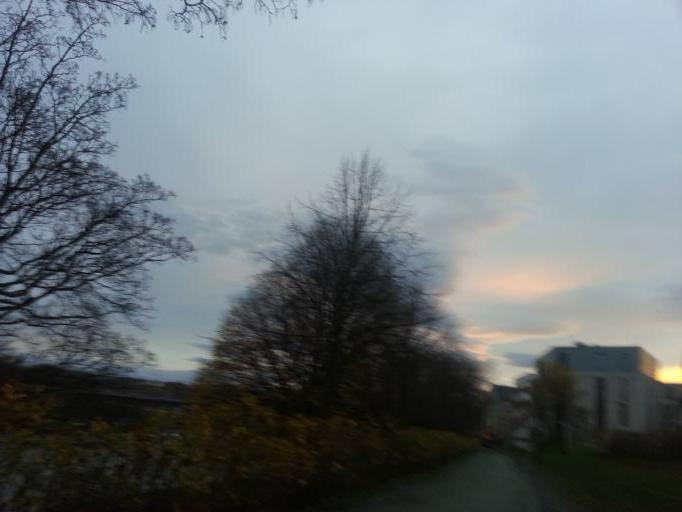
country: NO
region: Sor-Trondelag
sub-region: Trondheim
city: Trondheim
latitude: 63.4240
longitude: 10.3878
